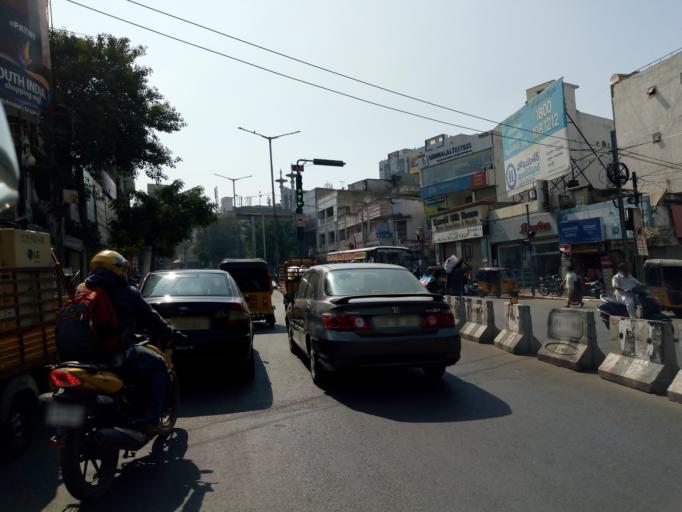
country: IN
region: Telangana
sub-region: Hyderabad
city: Malkajgiri
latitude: 17.4359
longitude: 78.4935
